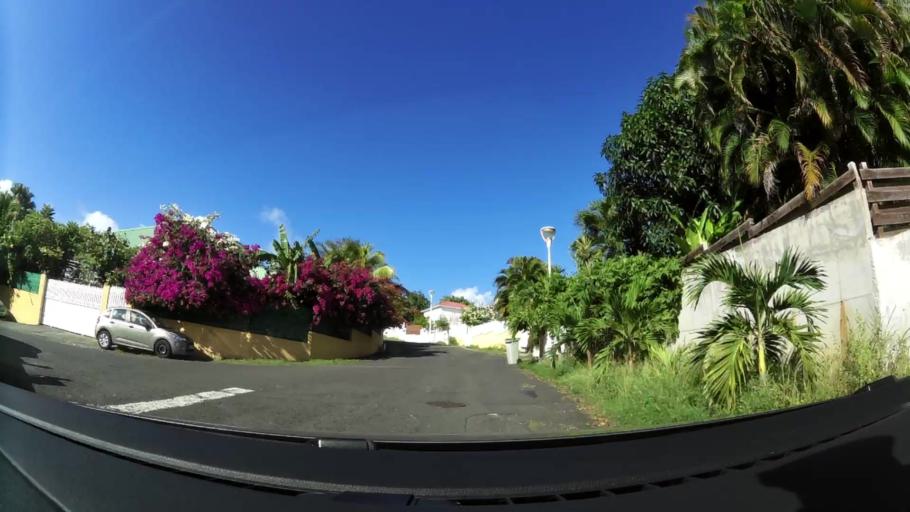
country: GP
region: Guadeloupe
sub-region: Guadeloupe
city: Le Gosier
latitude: 16.2021
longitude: -61.4699
